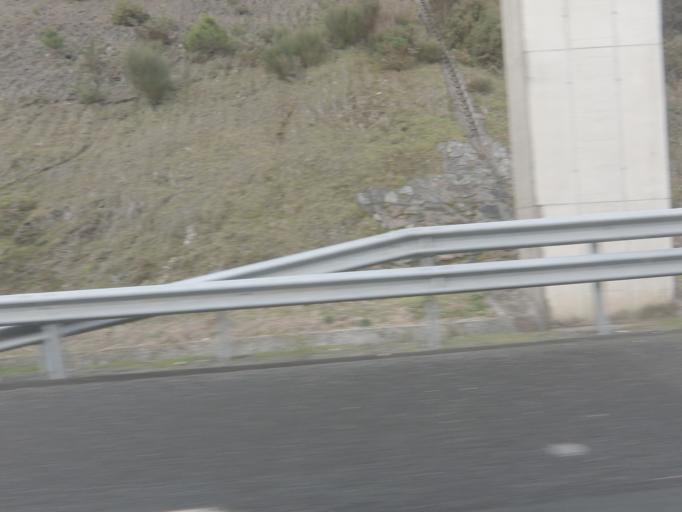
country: ES
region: Galicia
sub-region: Provincia de Pontevedra
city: Lalin
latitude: 42.6249
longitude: -8.1098
